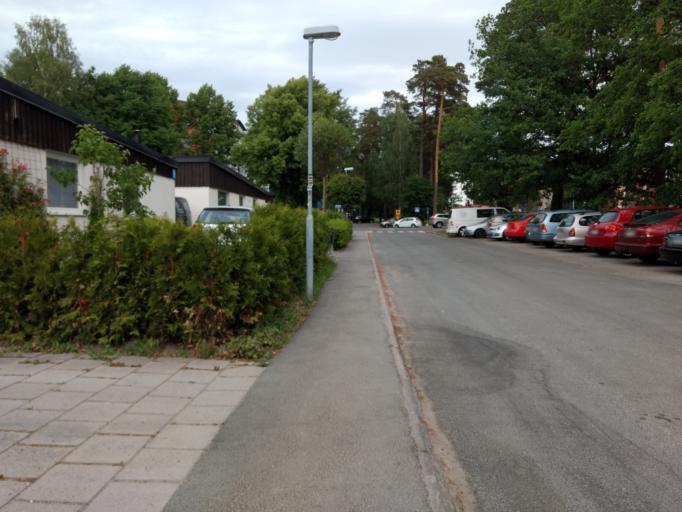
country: SE
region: Stockholm
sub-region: Upplands Vasby Kommun
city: Upplands Vaesby
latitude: 59.5241
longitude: 17.9145
